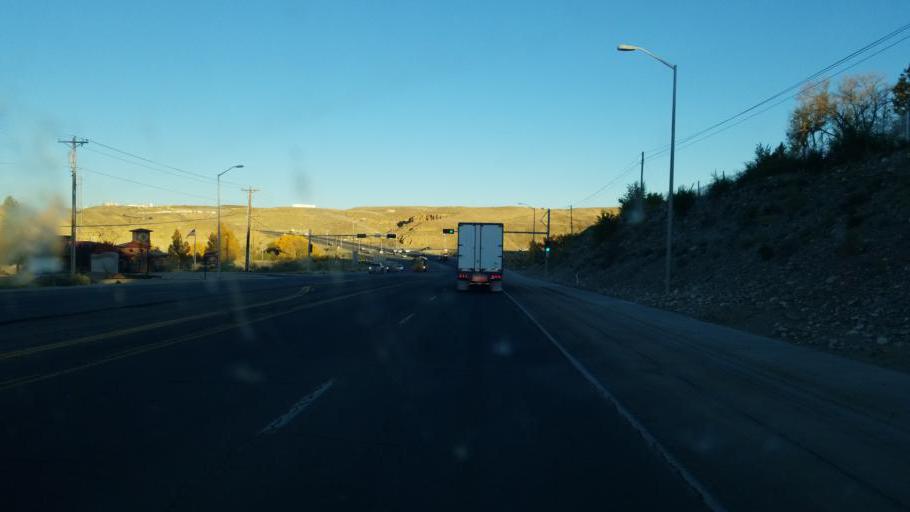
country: US
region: New Mexico
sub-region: San Juan County
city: Farmington
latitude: 36.7358
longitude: -108.2481
